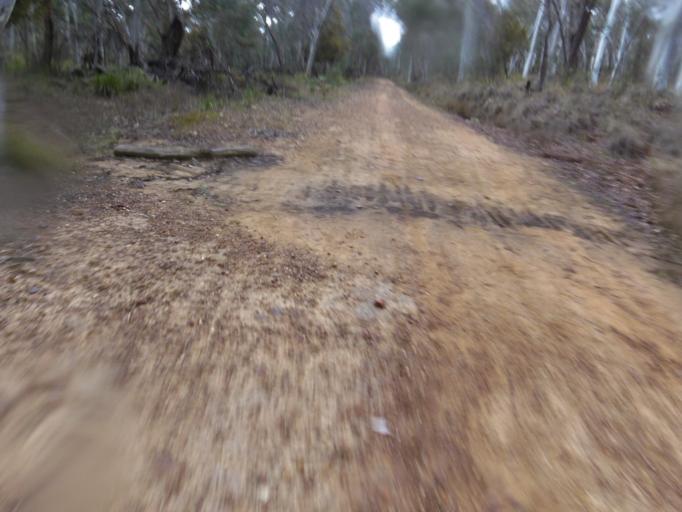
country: AU
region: Australian Capital Territory
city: Macquarie
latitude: -35.2667
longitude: 149.0889
